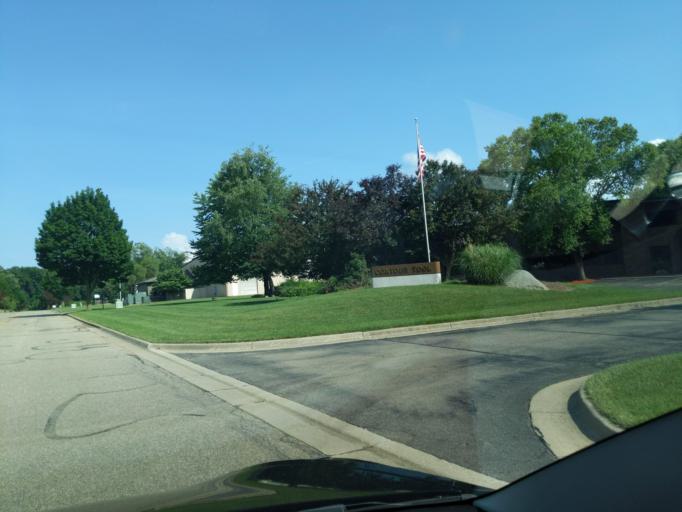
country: US
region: Michigan
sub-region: Jackson County
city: Jackson
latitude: 42.2299
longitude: -84.3710
